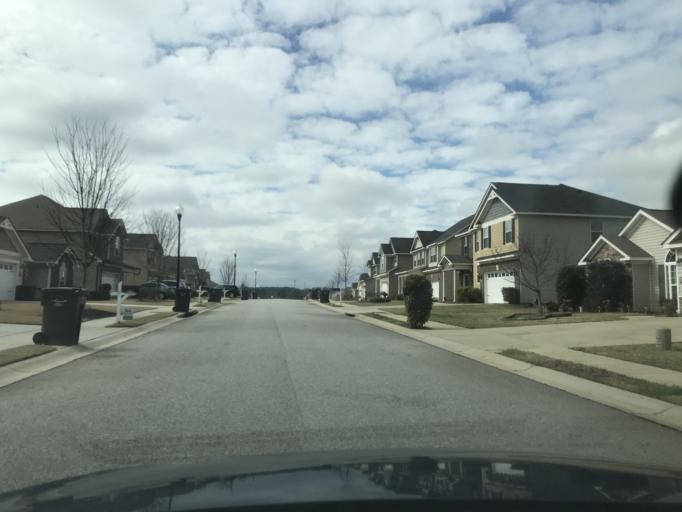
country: US
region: Georgia
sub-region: Columbia County
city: Grovetown
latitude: 33.4405
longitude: -82.1476
